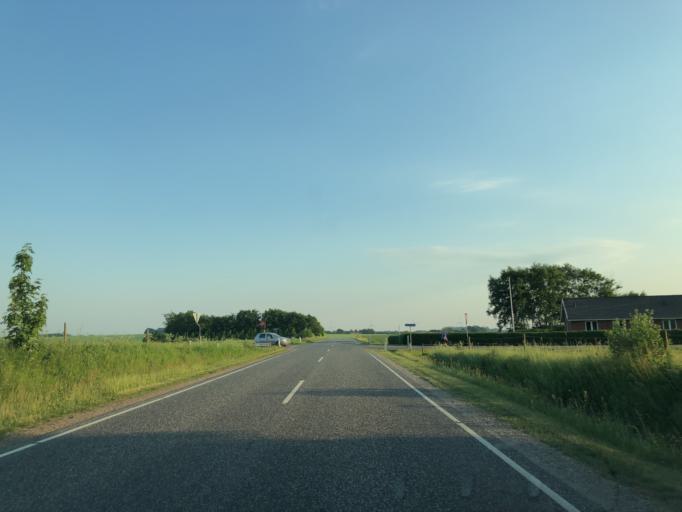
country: DK
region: Central Jutland
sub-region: Struer Kommune
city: Struer
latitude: 56.4475
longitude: 8.5353
